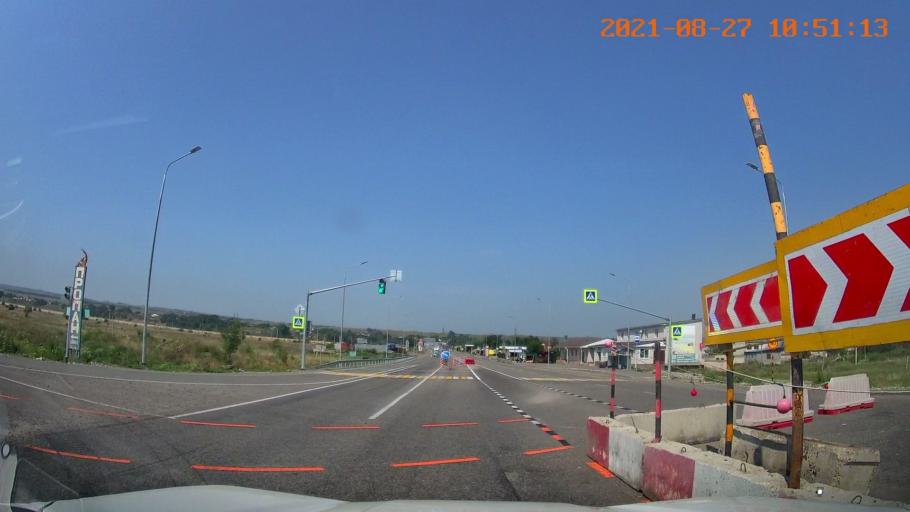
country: RU
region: Karachayevo-Cherkesiya
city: Adyge-Khabl'
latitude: 44.3608
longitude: 41.9425
